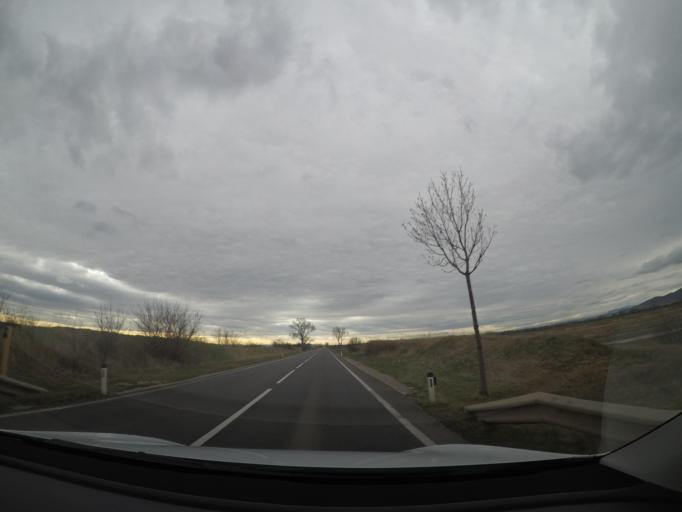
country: AT
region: Lower Austria
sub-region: Politischer Bezirk Modling
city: Hennersdorf
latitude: 48.1036
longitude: 16.3511
